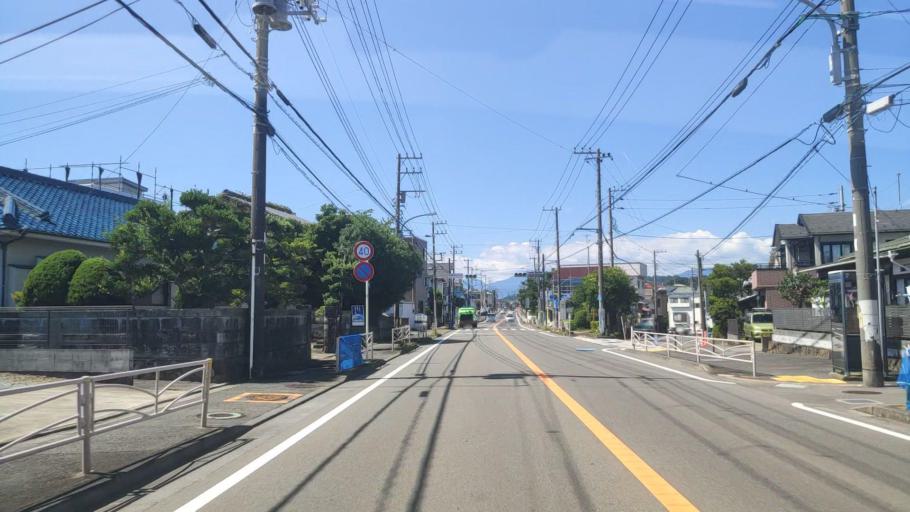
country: JP
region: Kanagawa
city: Ninomiya
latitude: 35.2953
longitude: 139.2515
